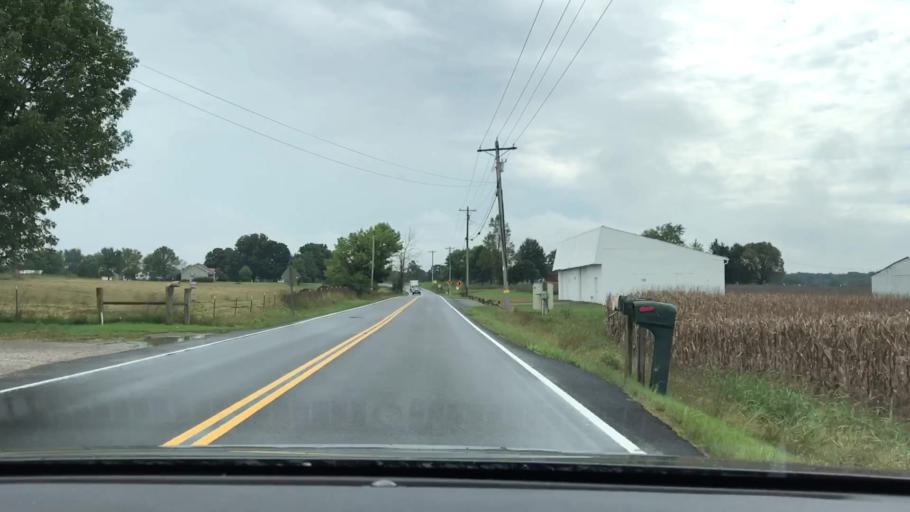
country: US
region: Tennessee
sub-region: Macon County
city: Red Boiling Springs
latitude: 36.5036
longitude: -85.8658
